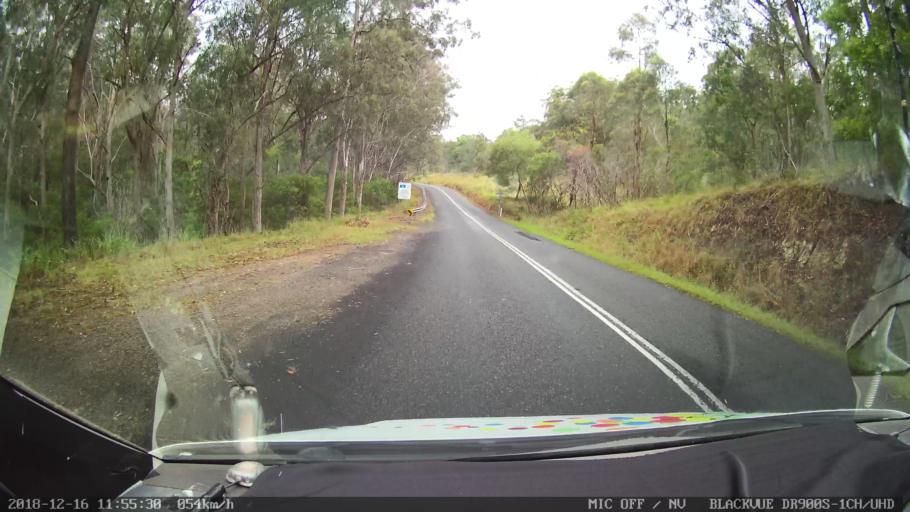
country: AU
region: New South Wales
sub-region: Tenterfield Municipality
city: Carrolls Creek
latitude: -28.9133
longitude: 152.2917
